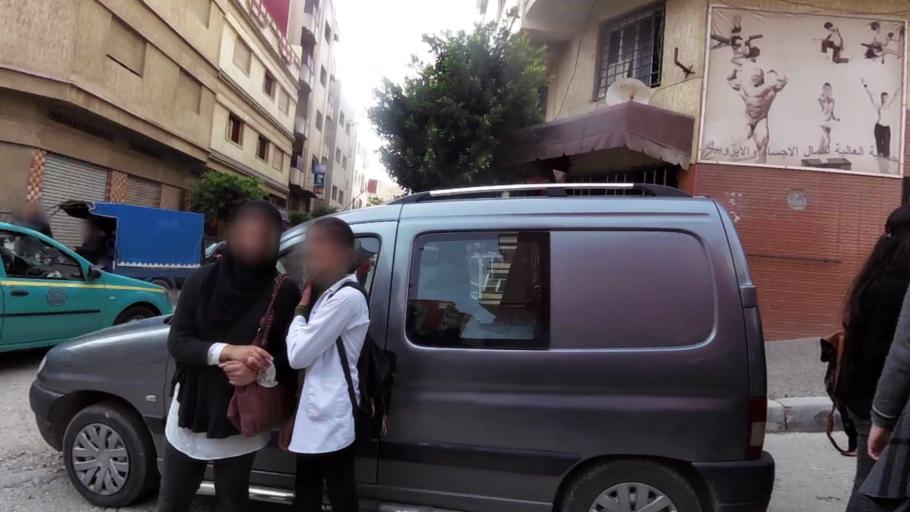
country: MA
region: Tanger-Tetouan
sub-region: Tanger-Assilah
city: Tangier
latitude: 35.7634
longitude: -5.7935
